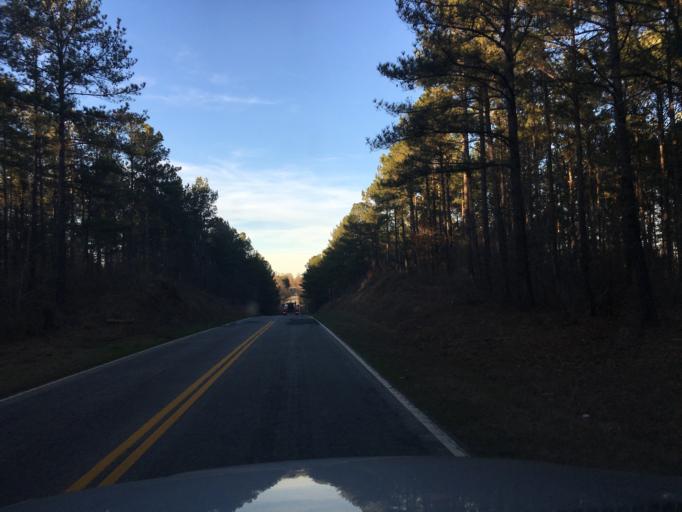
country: US
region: South Carolina
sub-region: Greenwood County
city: Ninety Six
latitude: 34.2214
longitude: -81.8788
